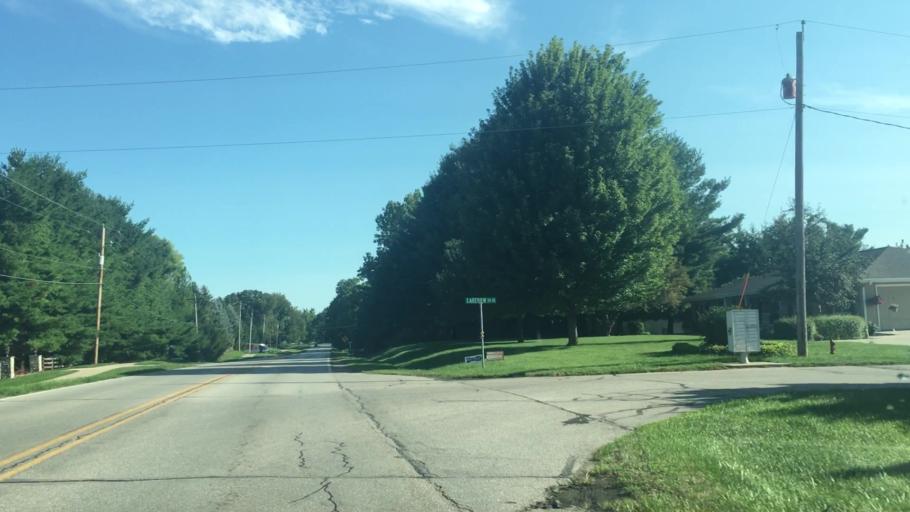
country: US
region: Iowa
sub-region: Johnson County
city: Coralville
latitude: 41.7114
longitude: -91.5508
